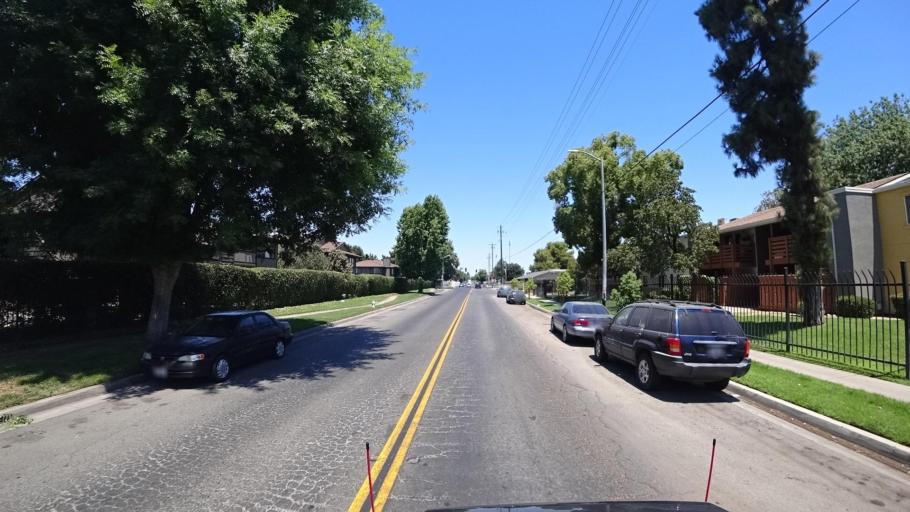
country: US
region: California
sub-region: Fresno County
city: Sunnyside
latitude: 36.7310
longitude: -119.7320
